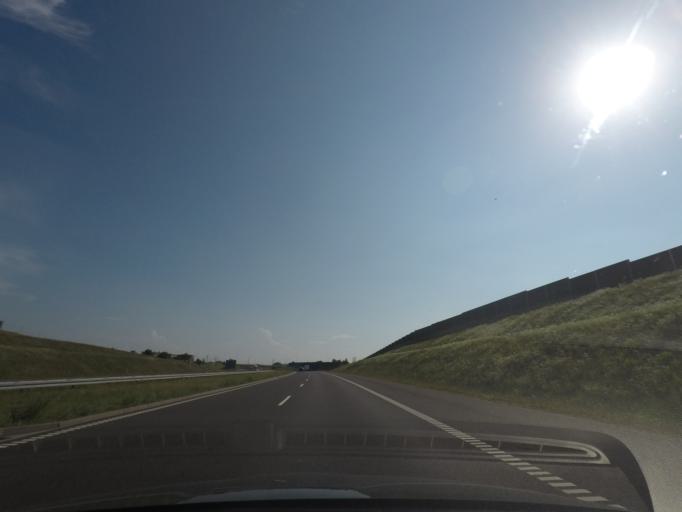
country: PL
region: Silesian Voivodeship
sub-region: Powiat rybnicki
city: Swierklany Gorne
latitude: 50.0360
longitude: 18.6049
